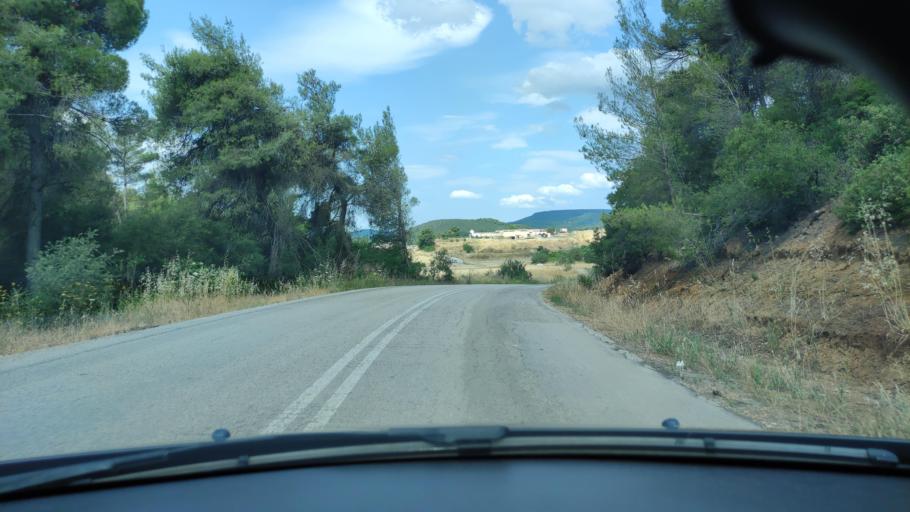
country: GR
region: Central Greece
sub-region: Nomos Evvoias
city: Afration
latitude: 38.5193
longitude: 23.7415
